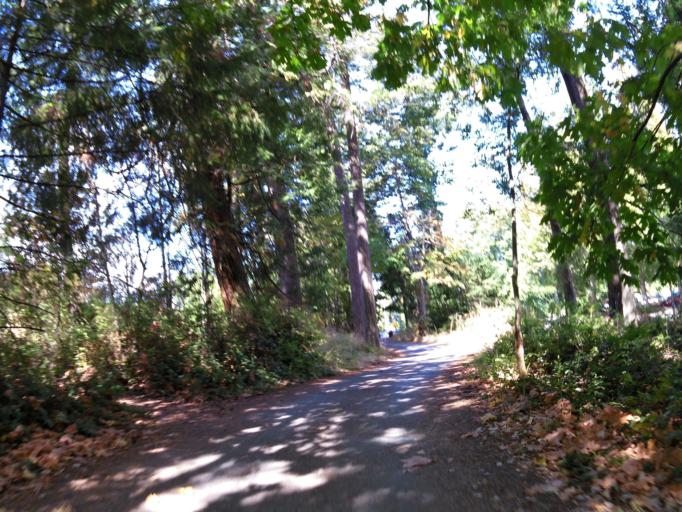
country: CA
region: British Columbia
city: Victoria
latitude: 48.5294
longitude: -123.3739
